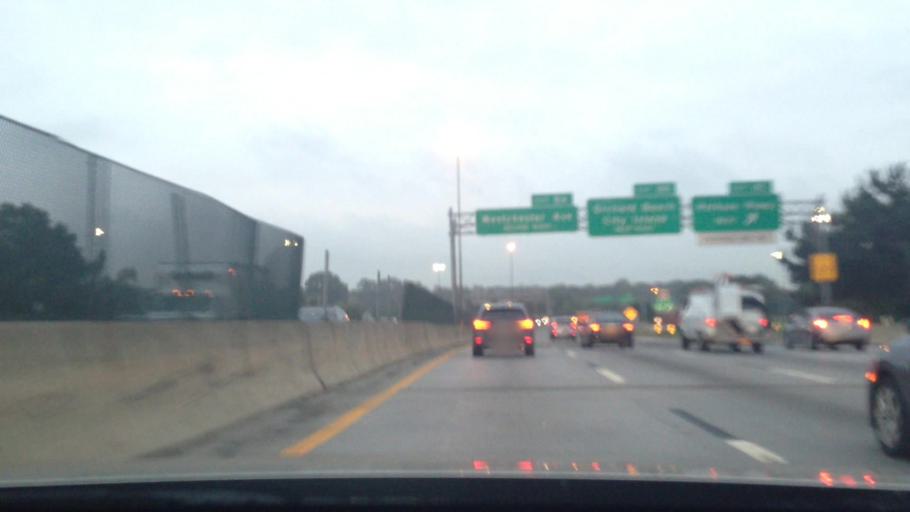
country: US
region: New York
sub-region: Bronx
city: Eastchester
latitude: 40.8591
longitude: -73.8272
